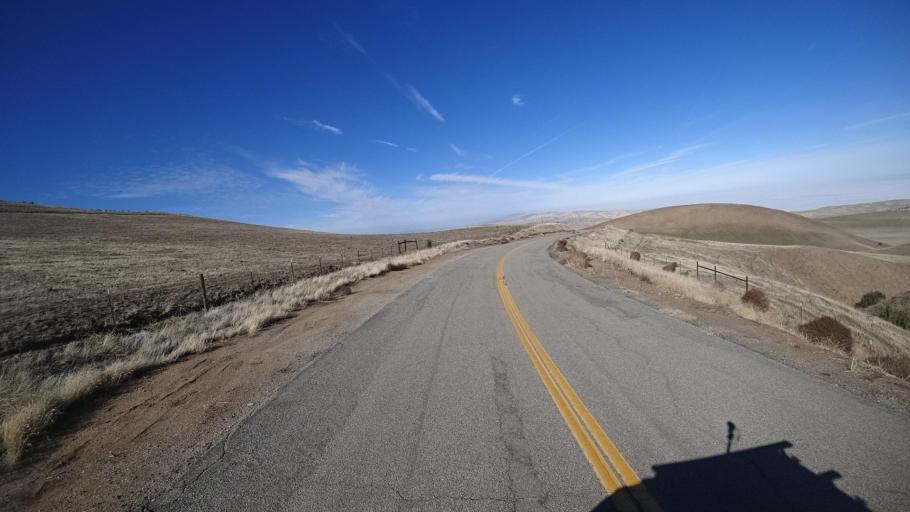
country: US
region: California
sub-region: Kern County
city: Maricopa
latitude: 34.9291
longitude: -119.4079
